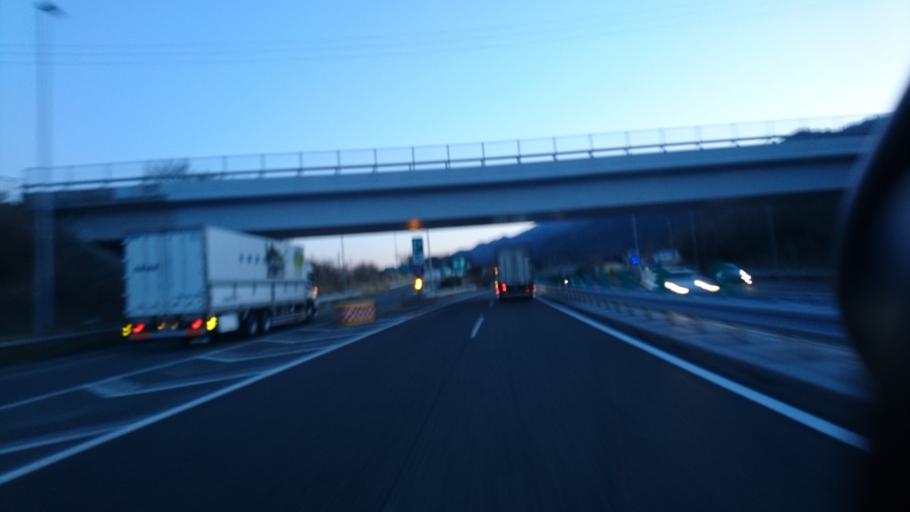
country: JP
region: Nagano
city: Ina
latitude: 35.8430
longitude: 137.9344
